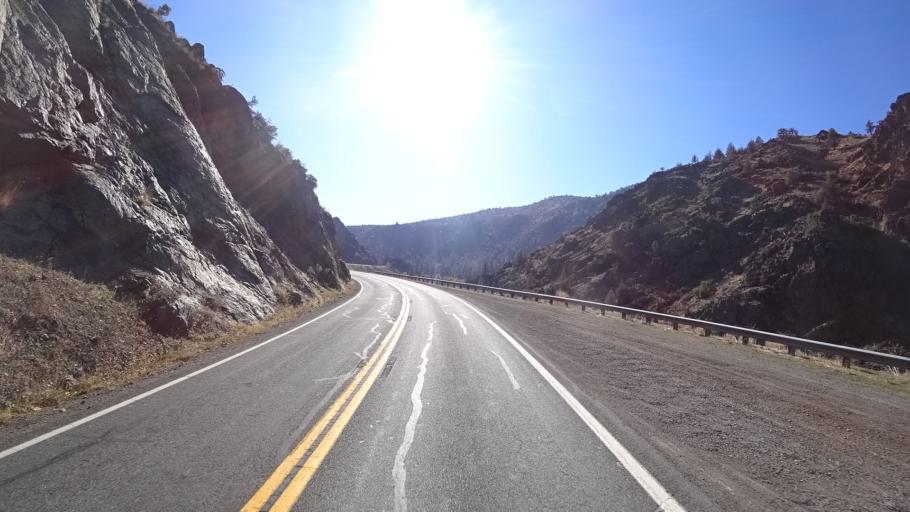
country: US
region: California
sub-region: Siskiyou County
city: Yreka
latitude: 41.8283
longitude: -122.5937
